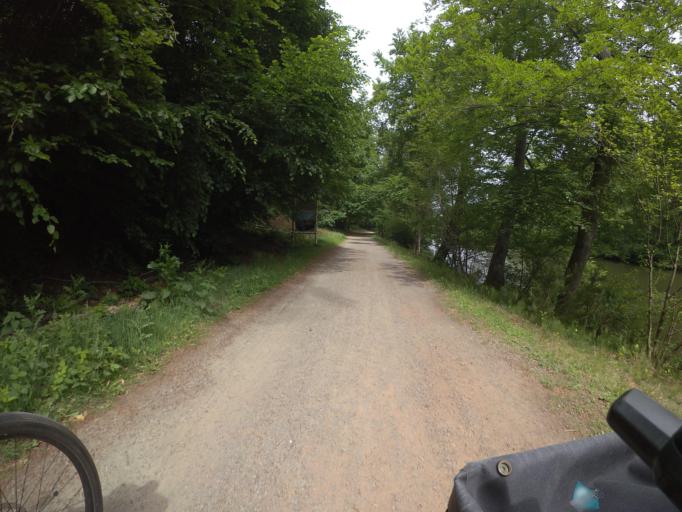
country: DE
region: Rheinland-Pfalz
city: Otterbach
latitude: 49.4494
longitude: 7.7343
